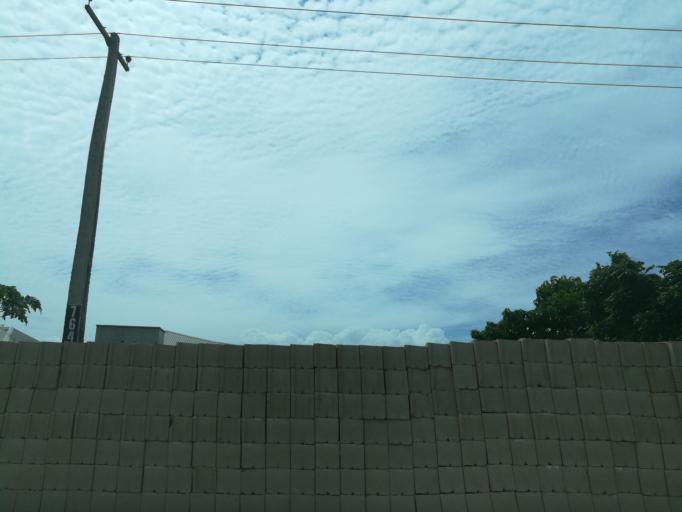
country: NG
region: Lagos
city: Ebute Ikorodu
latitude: 6.5614
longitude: 3.4764
